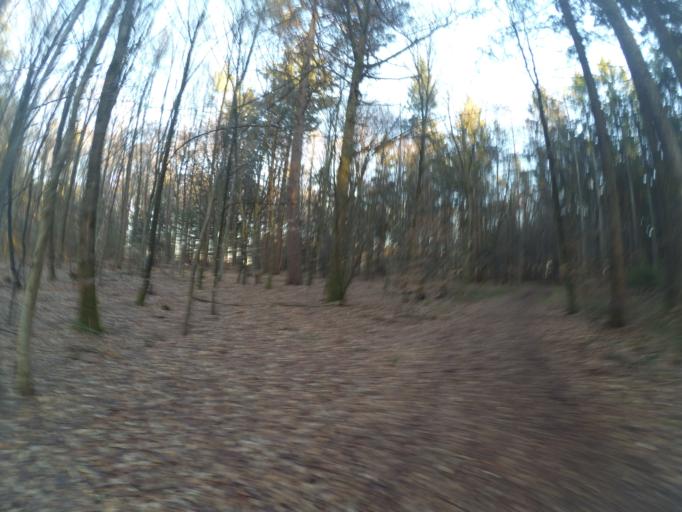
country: DE
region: Bavaria
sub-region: Swabia
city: Guenzburg
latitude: 48.4462
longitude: 10.3067
